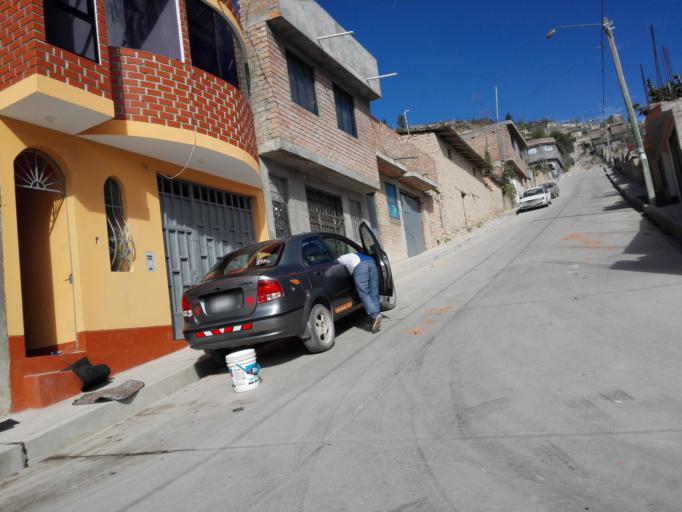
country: PE
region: Ayacucho
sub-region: Provincia de Huamanga
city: Ayacucho
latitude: -13.1381
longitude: -74.2341
